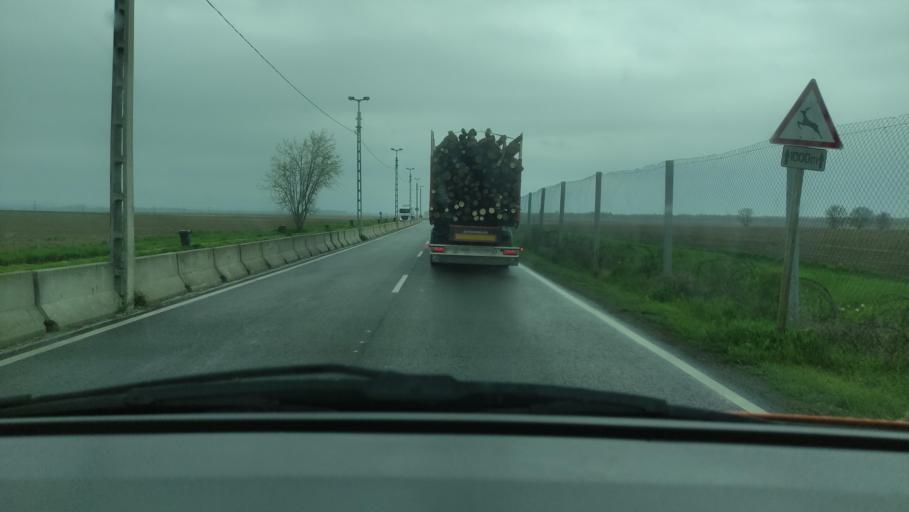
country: HU
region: Baranya
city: Mohacs
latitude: 45.9063
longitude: 18.6597
